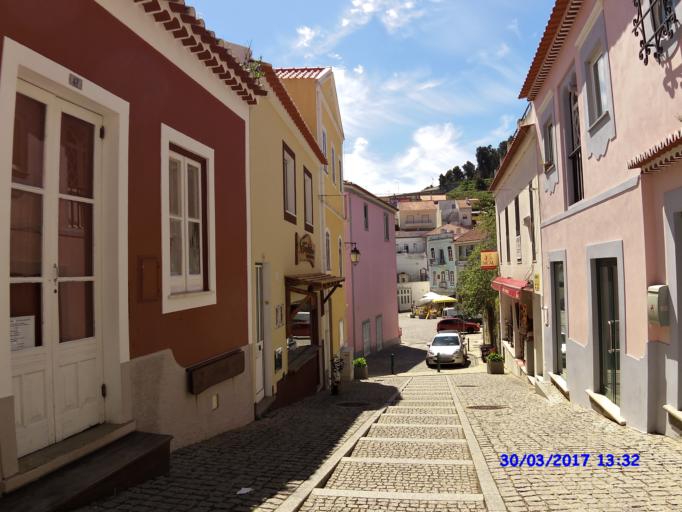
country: PT
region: Faro
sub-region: Monchique
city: Monchique
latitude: 37.3185
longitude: -8.5565
